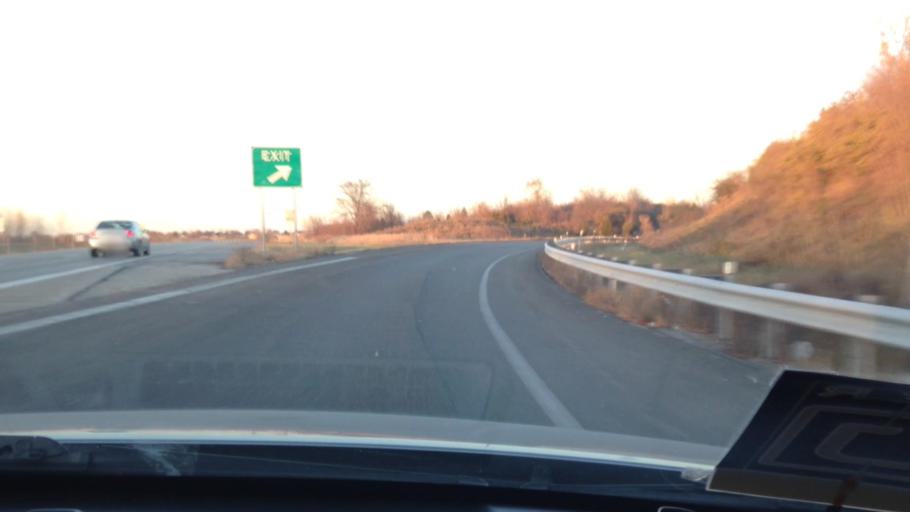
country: US
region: Missouri
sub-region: Clay County
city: Gladstone
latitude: 39.2557
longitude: -94.5891
